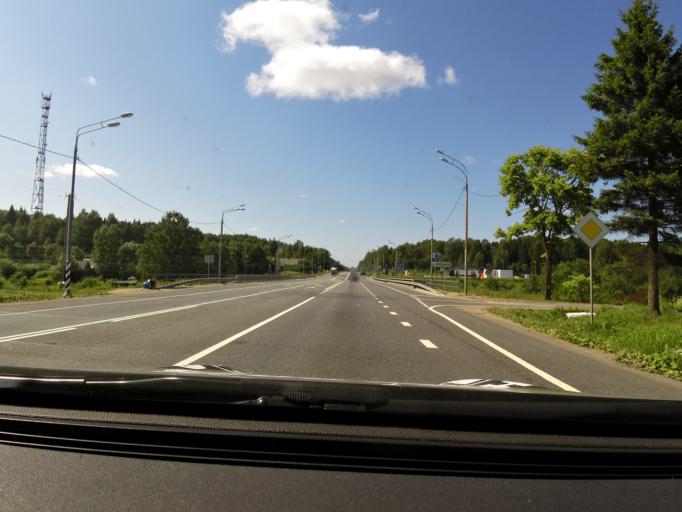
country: RU
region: Novgorod
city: Kresttsy
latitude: 58.3260
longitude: 32.3202
